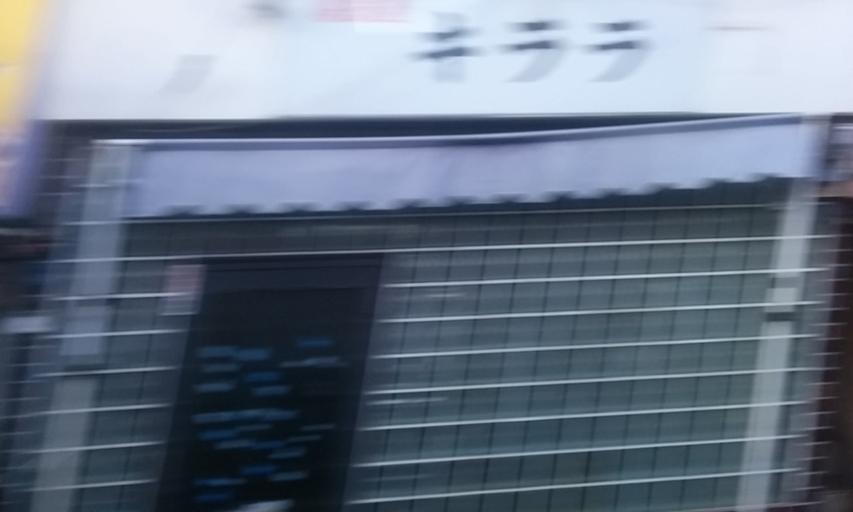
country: JP
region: Saitama
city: Kawaguchi
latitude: 35.7497
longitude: 139.7014
